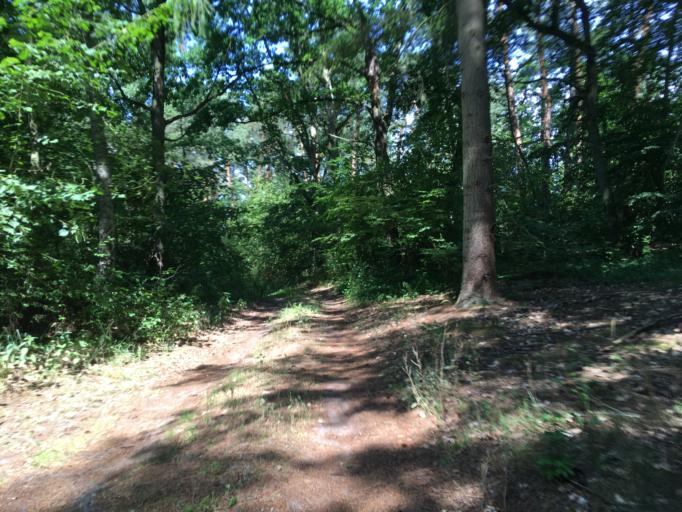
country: DE
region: Brandenburg
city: Zichow
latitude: 53.2359
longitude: 14.1178
